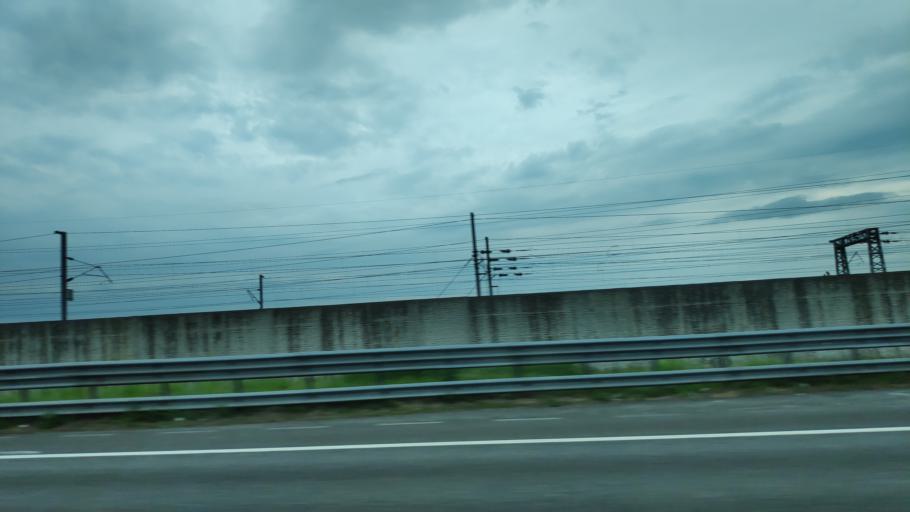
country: IT
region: Emilia-Romagna
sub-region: Provincia di Parma
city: Fidenza
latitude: 44.9075
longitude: 10.0254
